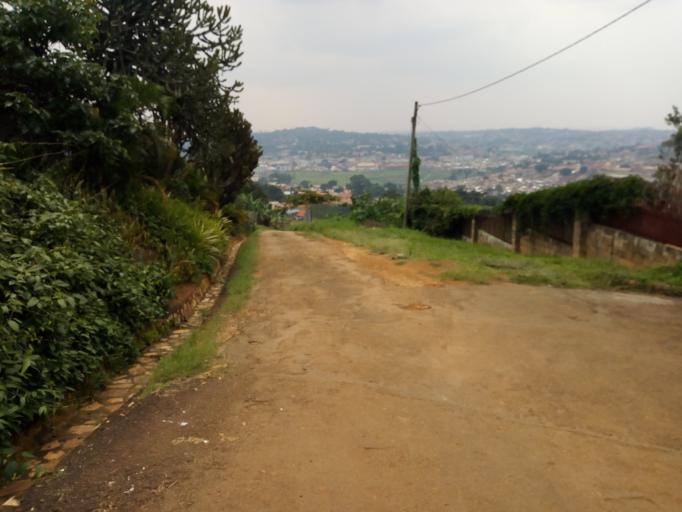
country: UG
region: Central Region
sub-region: Wakiso District
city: Kireka
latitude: 0.3271
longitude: 32.6325
